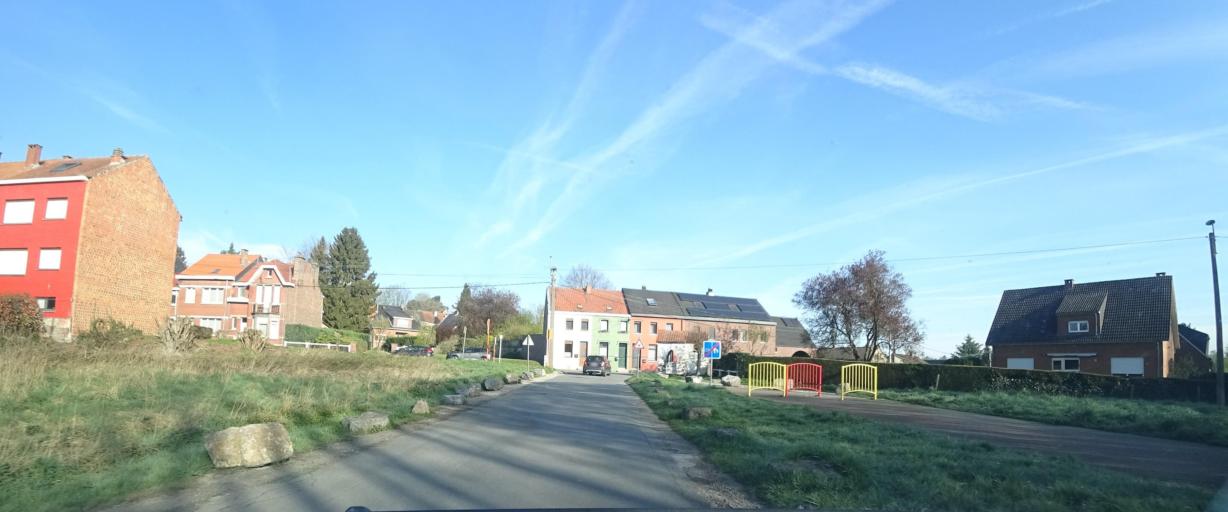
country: BE
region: Wallonia
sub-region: Province du Brabant Wallon
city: Braine-l'Alleud
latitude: 50.6888
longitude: 4.3855
